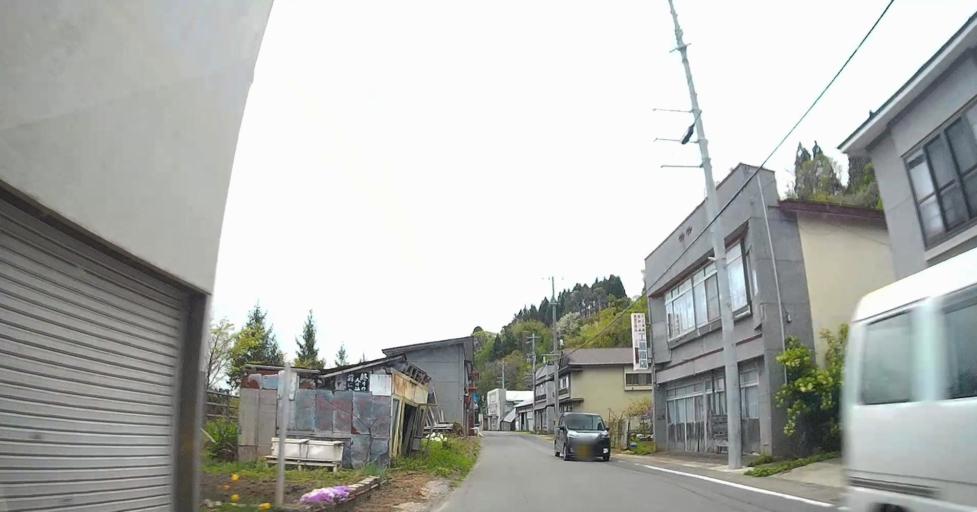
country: JP
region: Aomori
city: Shimokizukuri
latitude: 41.2043
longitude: 140.4271
